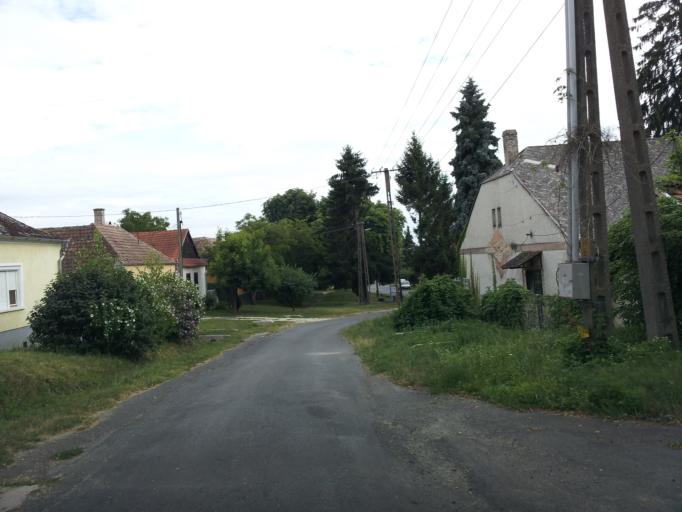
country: HU
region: Vas
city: Janoshaza
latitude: 47.1447
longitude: 17.1027
